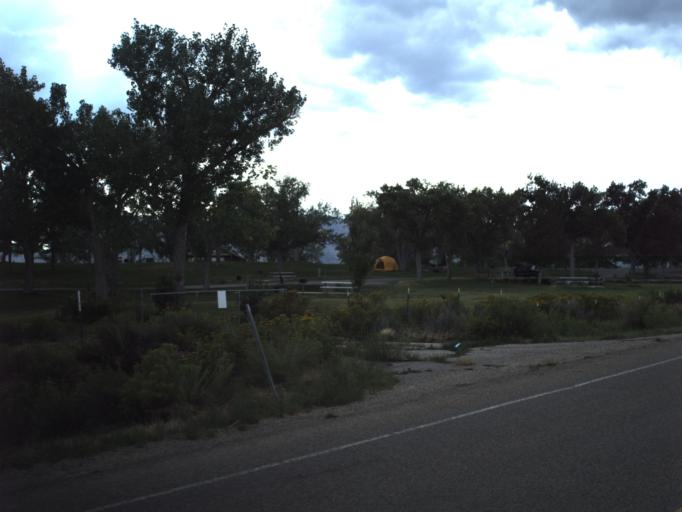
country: US
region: Utah
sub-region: Emery County
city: Huntington
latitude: 39.3460
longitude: -110.9405
